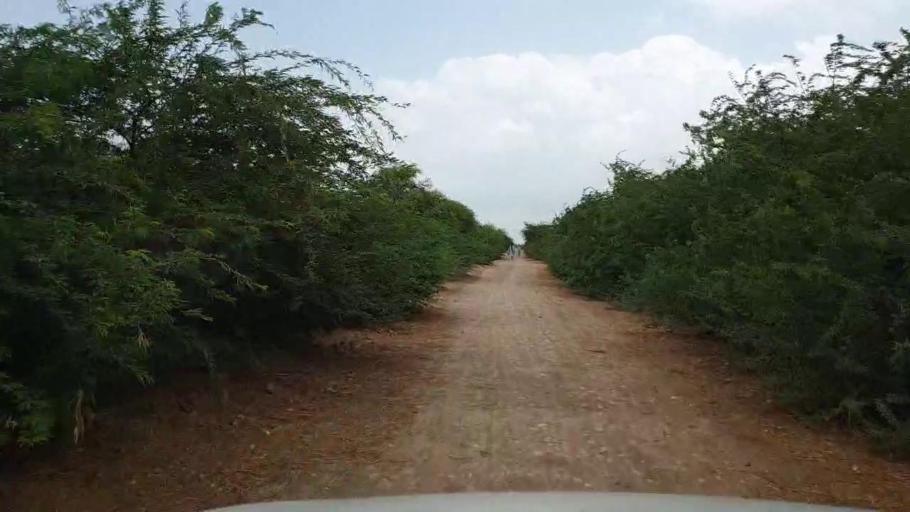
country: PK
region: Sindh
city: Kario
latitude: 24.6914
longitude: 68.6610
